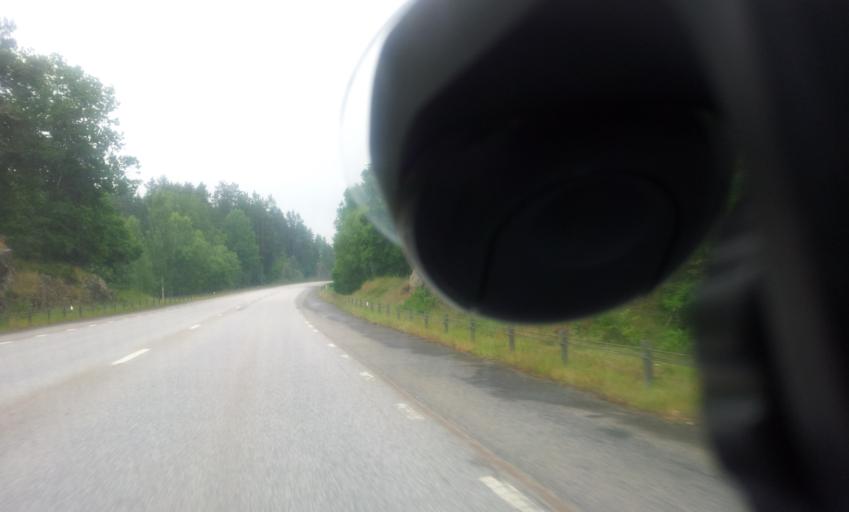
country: SE
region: Kalmar
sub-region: Vasterviks Kommun
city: Ankarsrum
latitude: 57.6797
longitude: 16.4436
